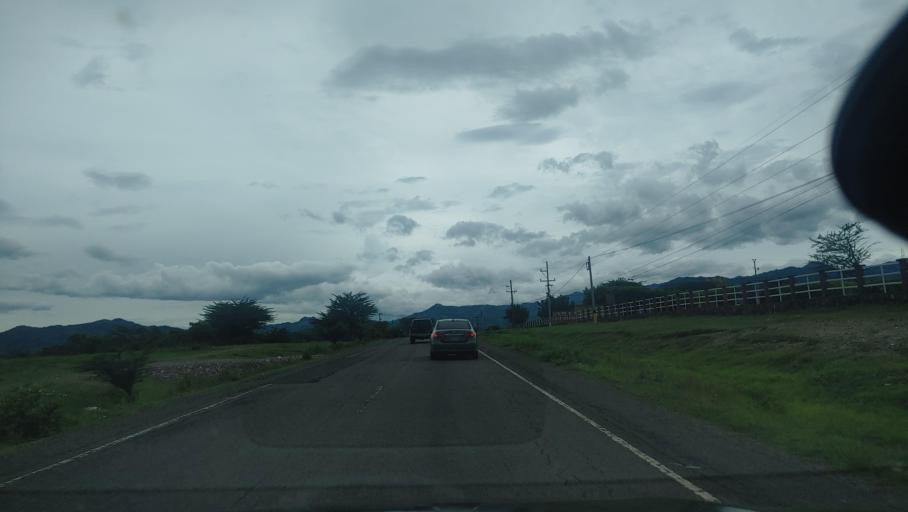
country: HN
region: Choluteca
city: Santa Ana de Yusguare
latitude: 13.3432
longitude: -87.1219
